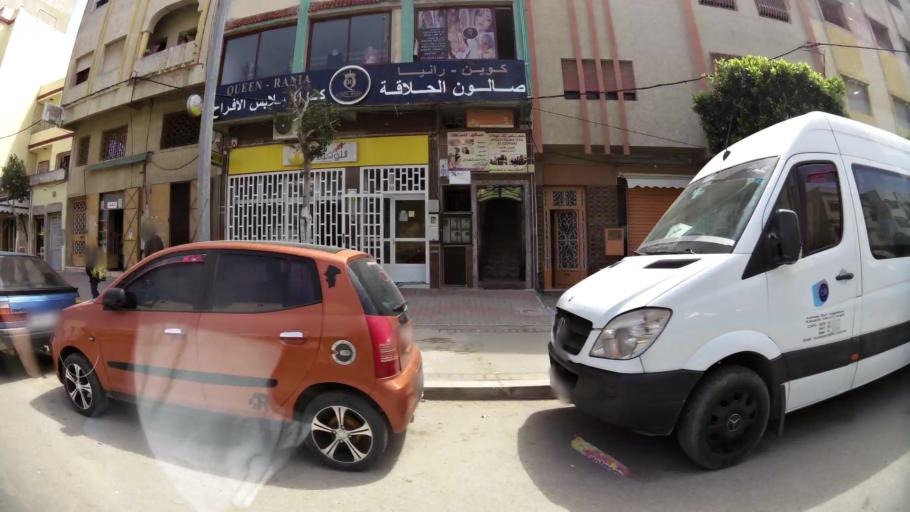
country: MA
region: Tanger-Tetouan
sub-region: Tanger-Assilah
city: Tangier
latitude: 35.7464
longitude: -5.8295
